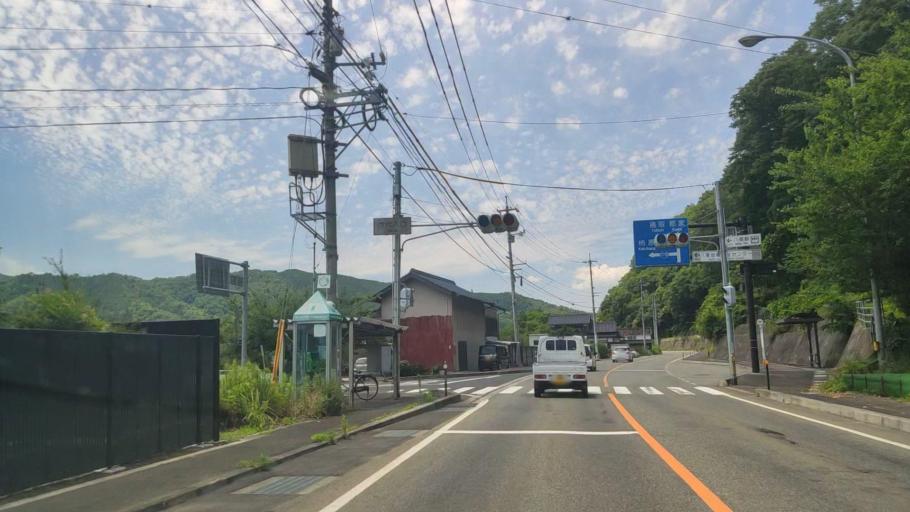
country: JP
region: Tottori
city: Tottori
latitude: 35.3663
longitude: 134.3201
